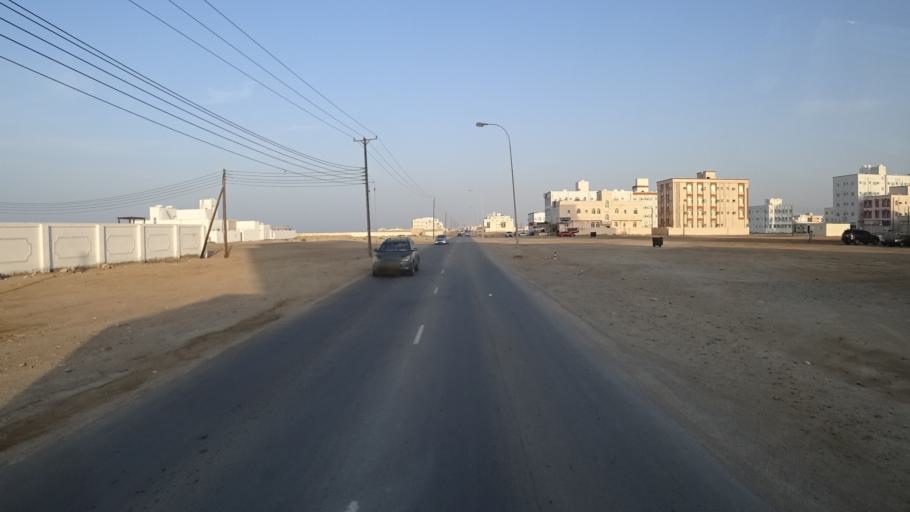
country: OM
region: Ash Sharqiyah
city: Sur
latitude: 22.6083
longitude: 59.4728
